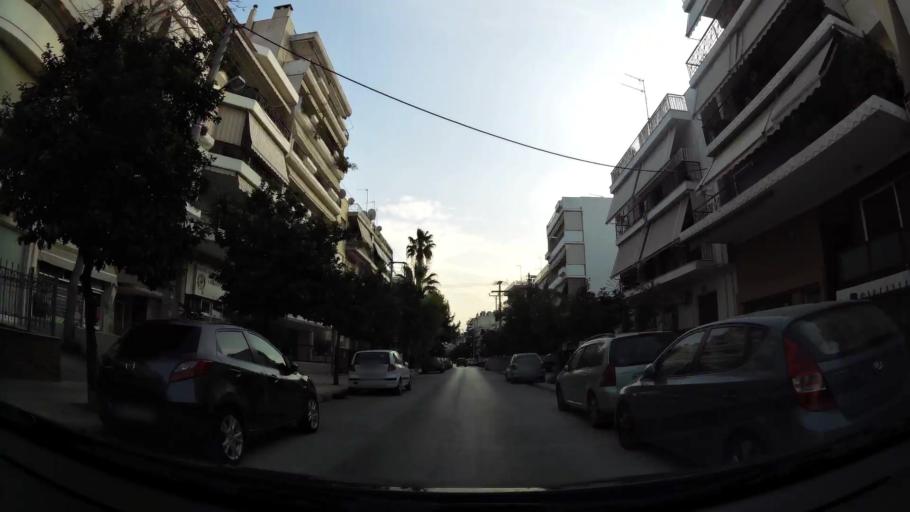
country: GR
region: Attica
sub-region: Nomarchia Athinas
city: Moskhaton
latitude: 37.9535
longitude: 23.6842
